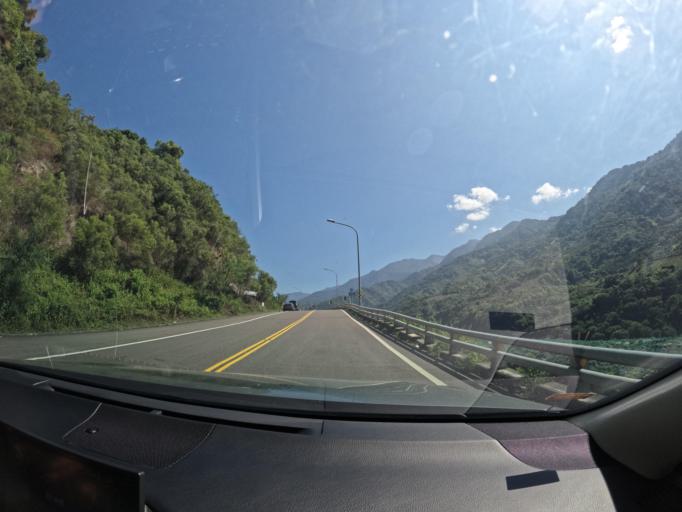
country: TW
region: Taiwan
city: Yujing
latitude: 23.1487
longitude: 120.7557
